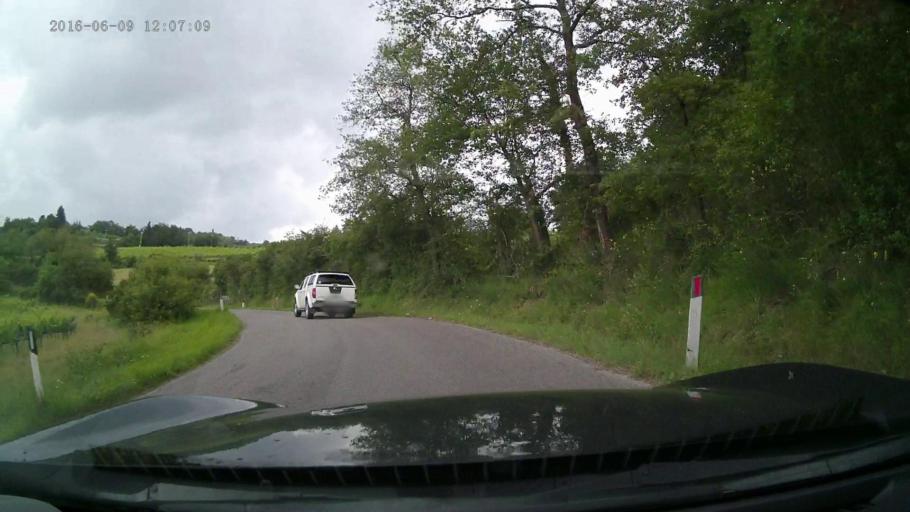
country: IT
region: Tuscany
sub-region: Province of Florence
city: Panzano in Chianti
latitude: 43.5276
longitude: 11.2859
